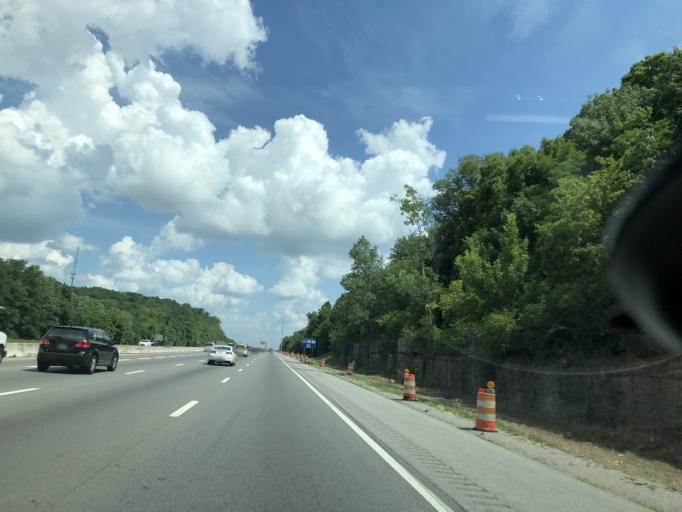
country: US
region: Tennessee
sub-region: Rutherford County
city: La Vergne
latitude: 36.0260
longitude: -86.6339
